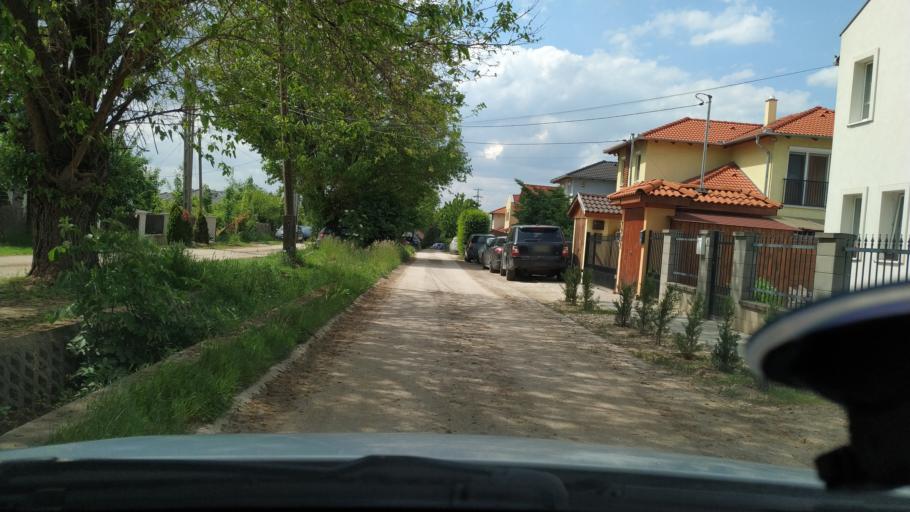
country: HU
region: Pest
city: Peteri
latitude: 47.4099
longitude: 19.4097
